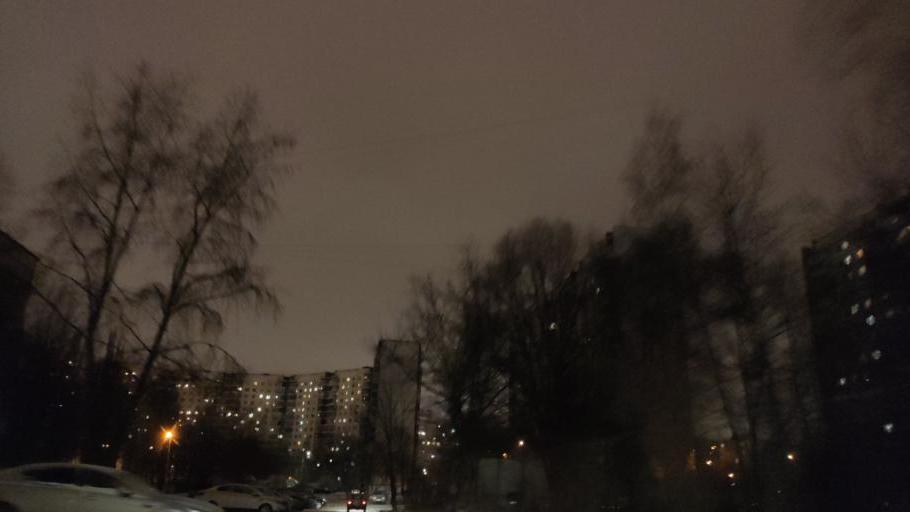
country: RU
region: Moscow
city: Tyoply Stan
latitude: 55.6271
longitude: 37.4837
